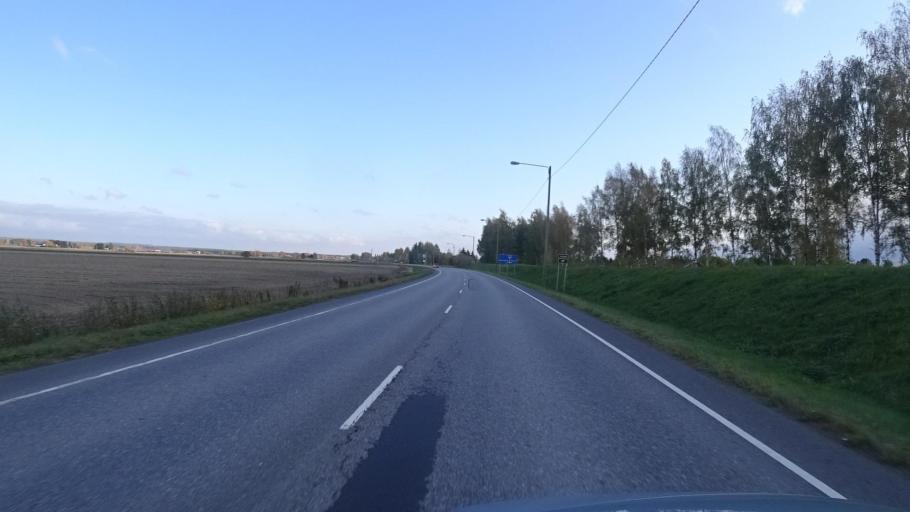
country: FI
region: Satakunta
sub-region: Rauma
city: Saekylae
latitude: 61.0568
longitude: 22.3296
